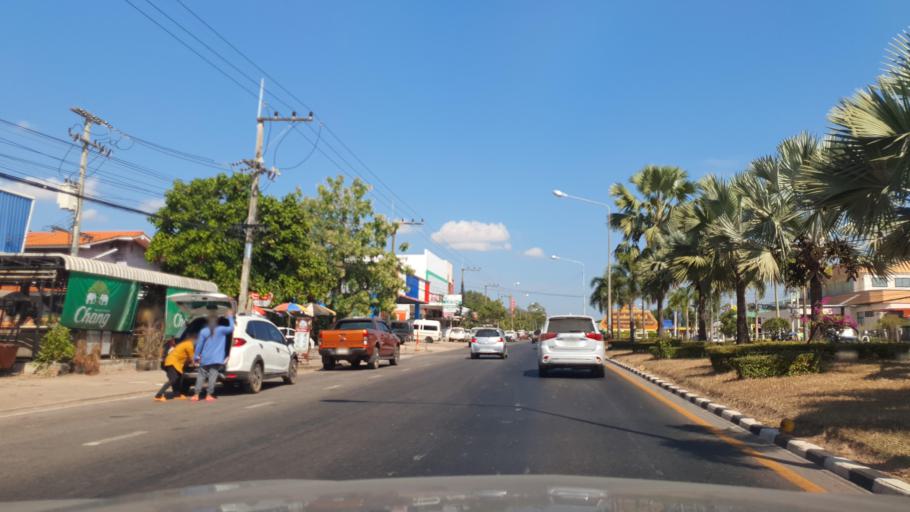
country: TH
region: Kalasin
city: Somdet
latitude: 16.7092
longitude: 103.7513
